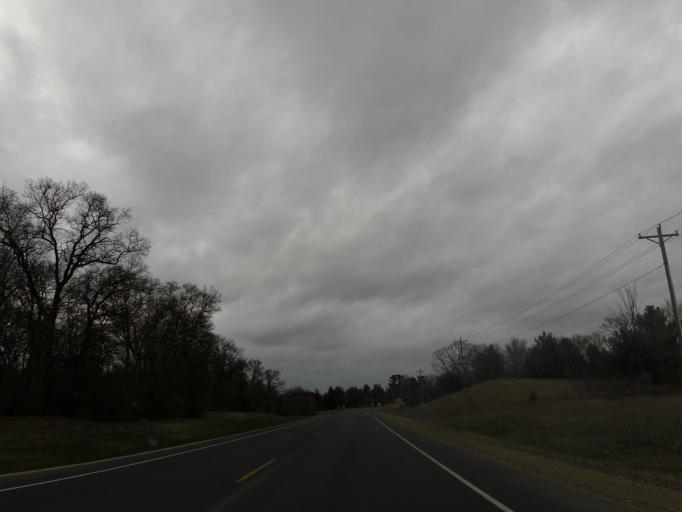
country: US
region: Wisconsin
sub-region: Saint Croix County
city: New Richmond
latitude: 45.1154
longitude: -92.5582
